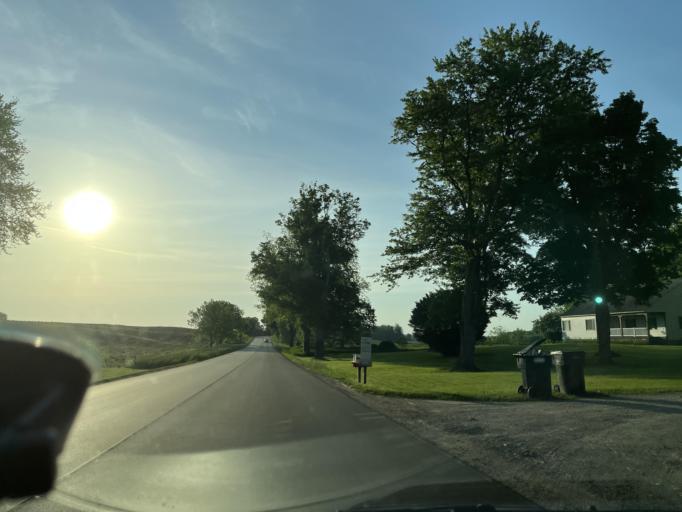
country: US
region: Michigan
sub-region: Barry County
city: Middleville
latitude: 42.7111
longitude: -85.4384
